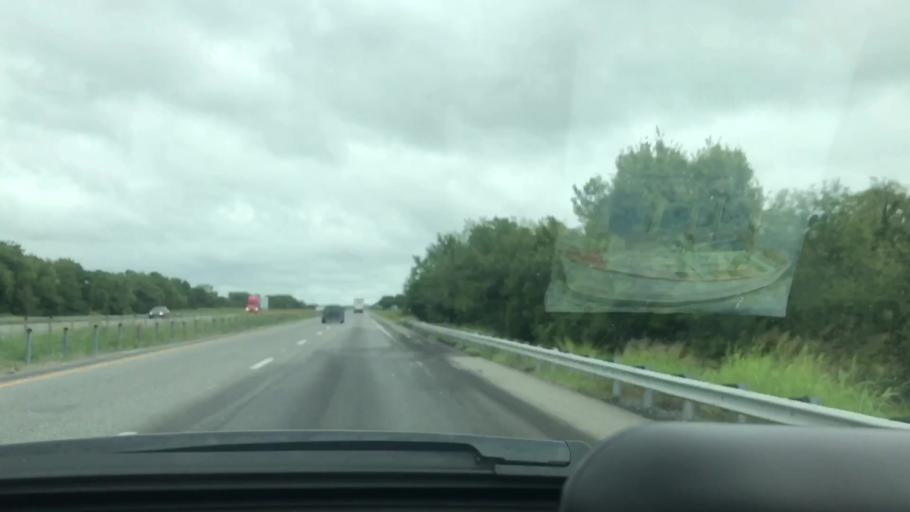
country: US
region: Oklahoma
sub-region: Pittsburg County
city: McAlester
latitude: 34.8049
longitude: -95.8643
